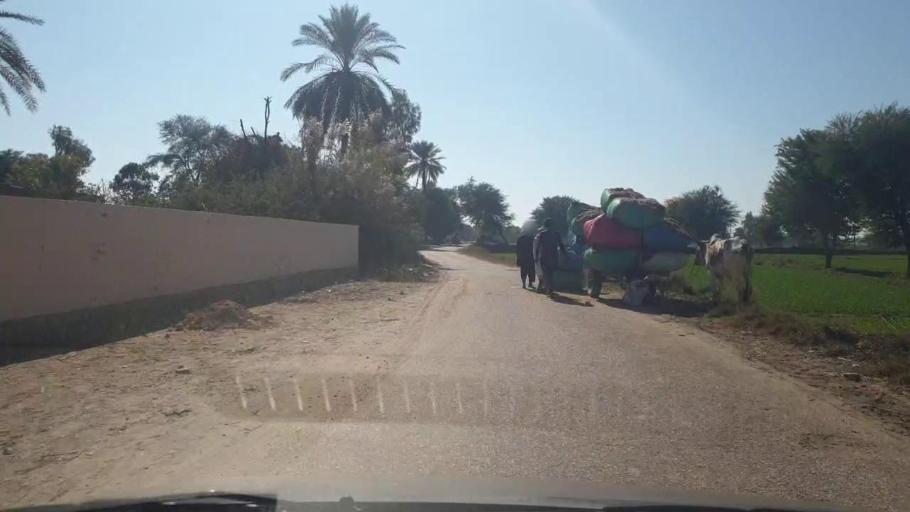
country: PK
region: Sindh
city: Bozdar
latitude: 27.1426
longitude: 68.6451
